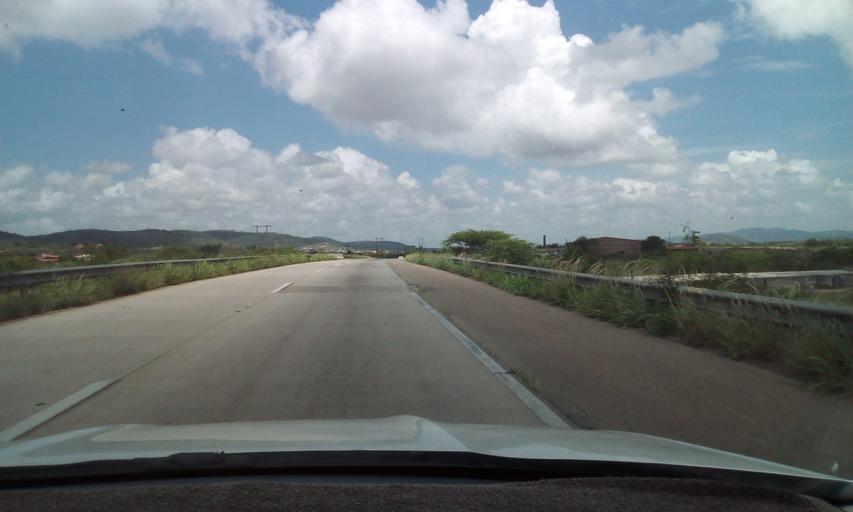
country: BR
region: Pernambuco
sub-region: Gravata
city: Gravata
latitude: -8.2124
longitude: -35.6185
